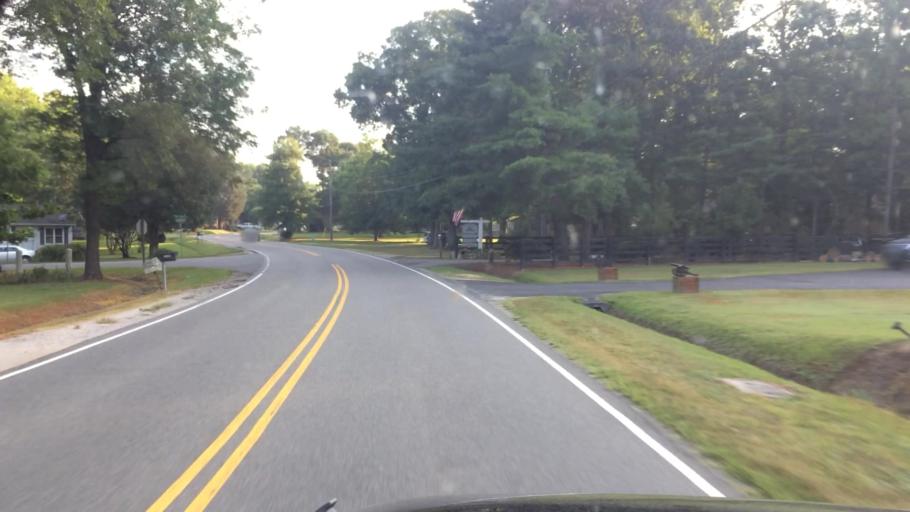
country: US
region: Virginia
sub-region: James City County
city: Williamsburg
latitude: 37.3257
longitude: -76.7355
